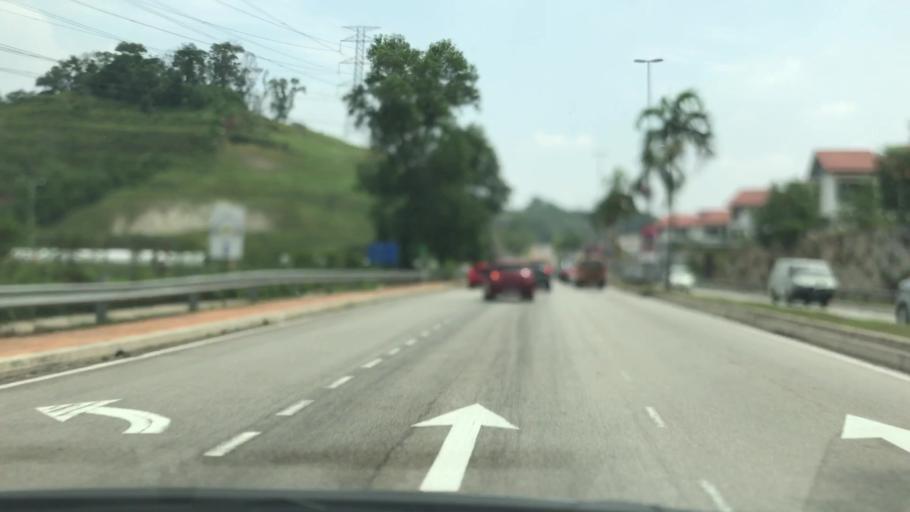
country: MY
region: Selangor
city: Kampong Baharu Balakong
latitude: 3.0355
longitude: 101.6775
